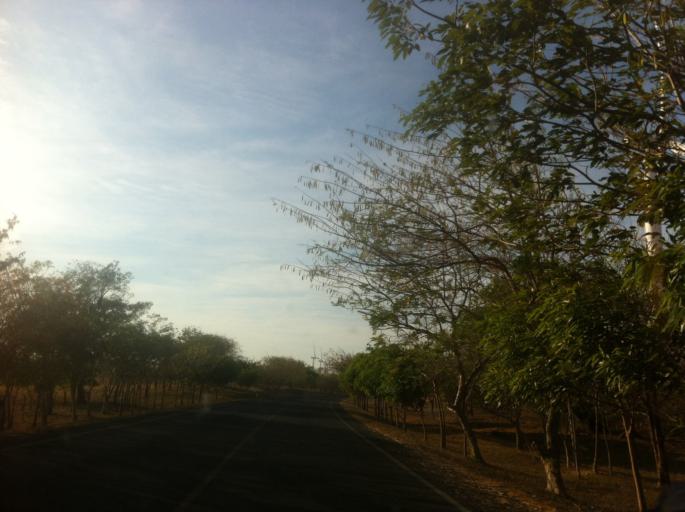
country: NI
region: Rivas
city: San Jorge
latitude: 11.3102
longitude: -85.6965
